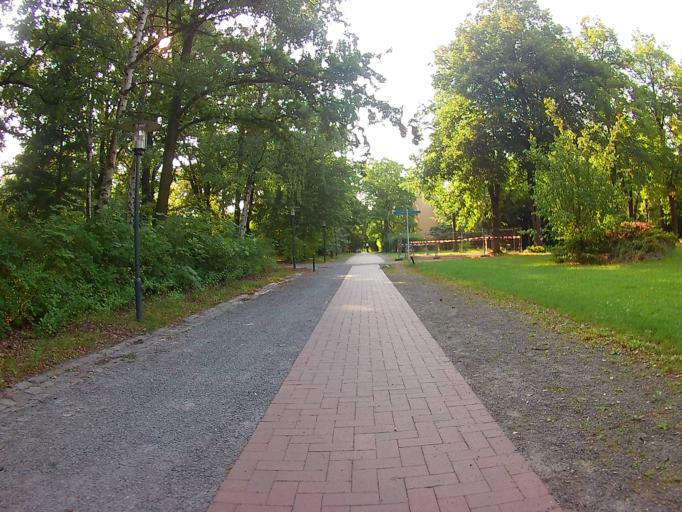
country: DE
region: Berlin
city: Biesdorf
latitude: 52.5150
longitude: 13.5681
